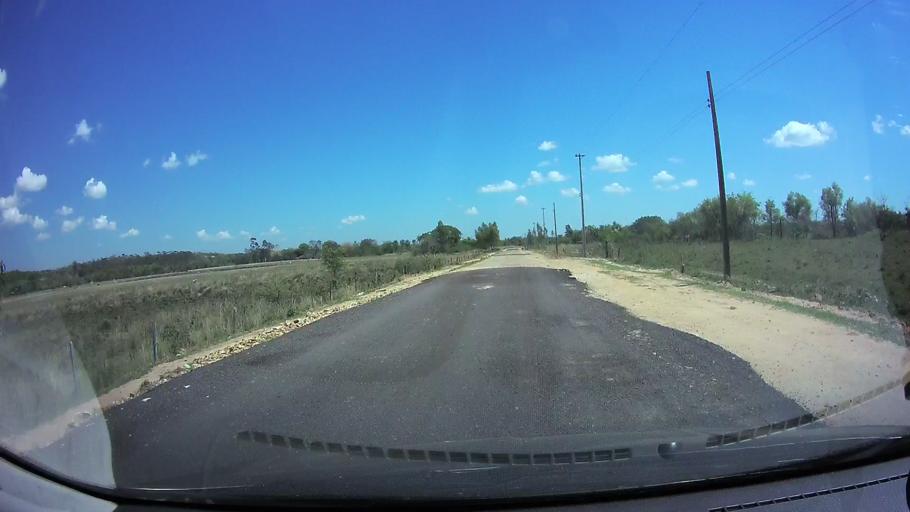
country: PY
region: Cordillera
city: Emboscada
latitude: -25.1371
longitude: -57.2664
